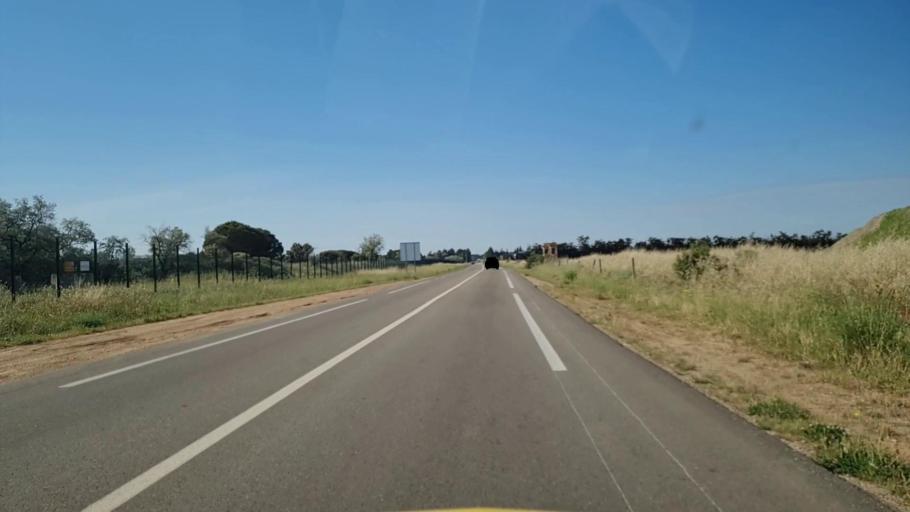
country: FR
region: Languedoc-Roussillon
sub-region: Departement du Gard
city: Garons
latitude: 43.7699
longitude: 4.4053
